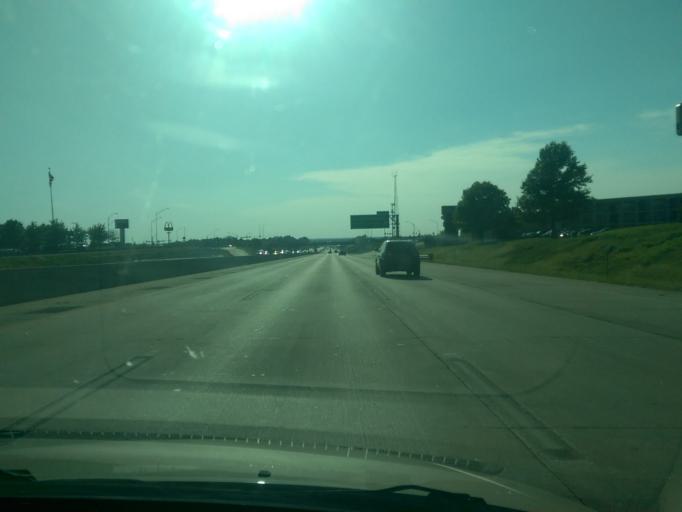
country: US
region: Missouri
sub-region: Jackson County
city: Blue Springs
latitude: 39.0338
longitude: -94.3006
